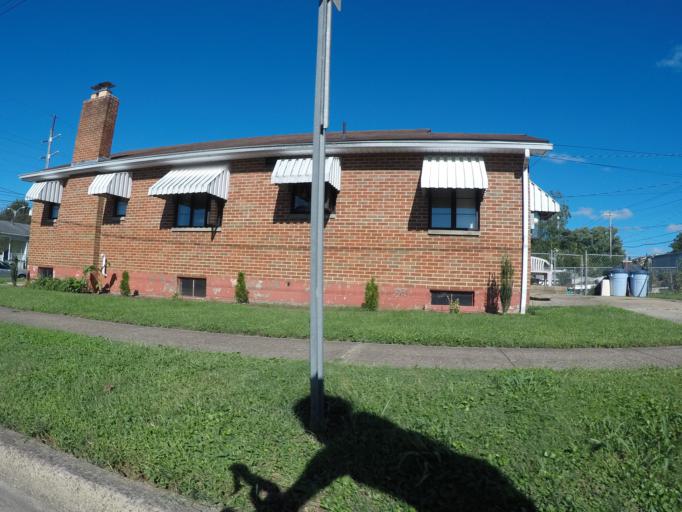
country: US
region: Ohio
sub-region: Lawrence County
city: Burlington
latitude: 38.4020
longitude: -82.5057
